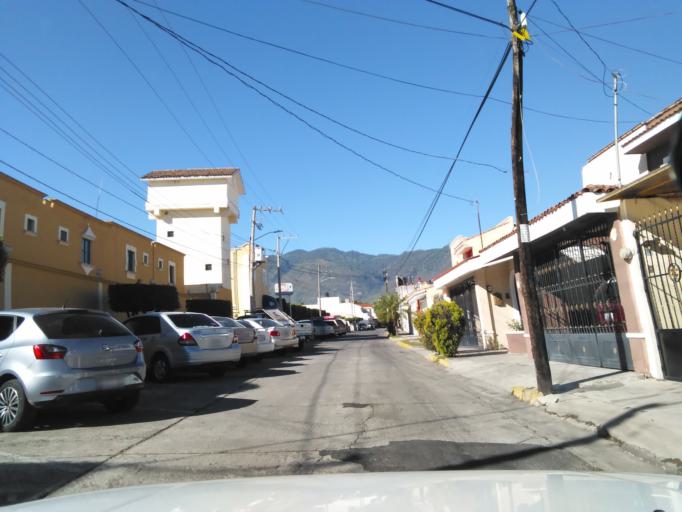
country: MX
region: Nayarit
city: Tepic
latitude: 21.4875
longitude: -104.8845
